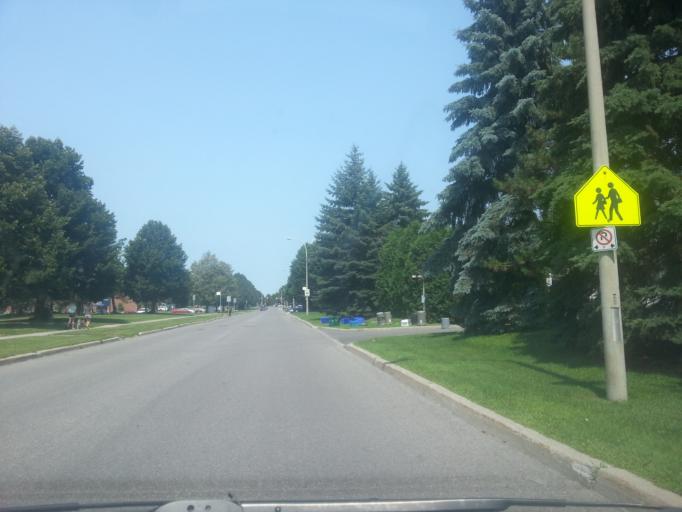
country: CA
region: Quebec
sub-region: Outaouais
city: Gatineau
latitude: 45.4788
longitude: -75.5299
